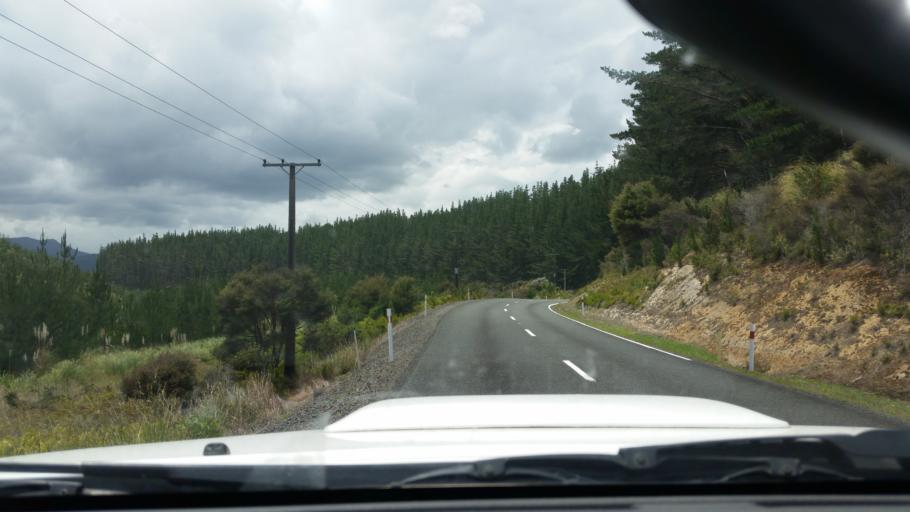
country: NZ
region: Northland
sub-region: Kaipara District
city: Dargaville
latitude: -35.8224
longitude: 173.7054
